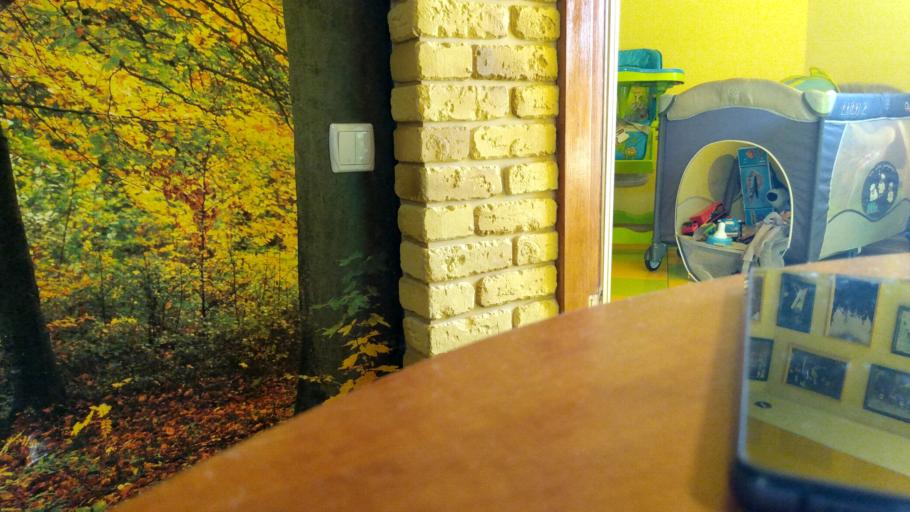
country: RU
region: Tverskaya
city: Likhoslavl'
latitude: 57.2058
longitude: 35.5082
